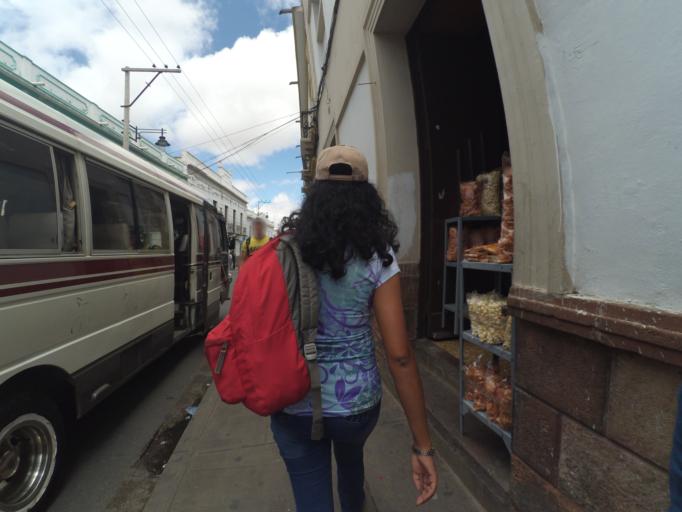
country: BO
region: Chuquisaca
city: Sucre
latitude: -19.0459
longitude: -65.2571
